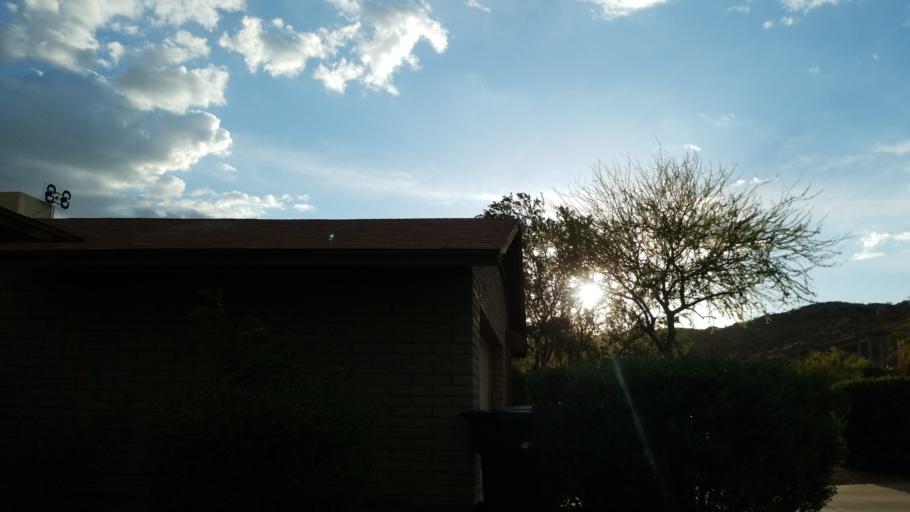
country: US
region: Arizona
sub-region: Maricopa County
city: Paradise Valley
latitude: 33.5894
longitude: -112.0546
